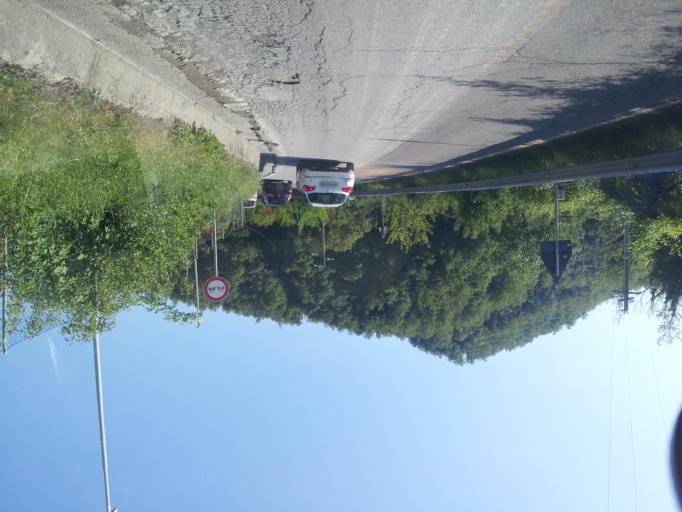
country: IT
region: Emilia-Romagna
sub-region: Provincia di Reggio Emilia
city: Casina
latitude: 44.5301
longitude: 10.5171
